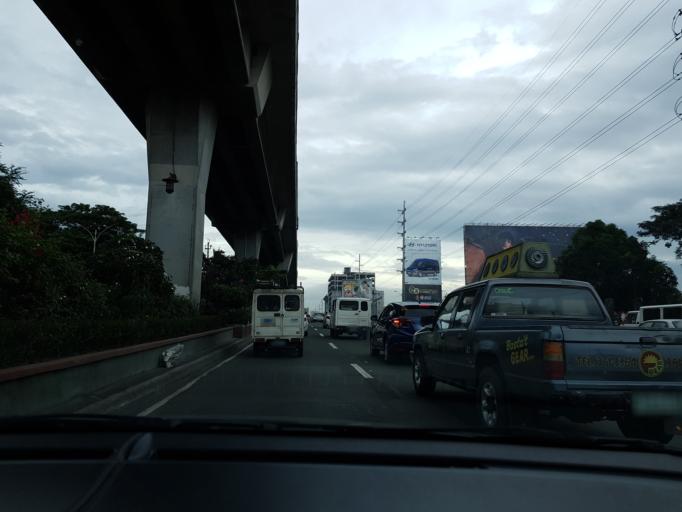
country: PH
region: Calabarzon
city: Del Monte
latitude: 14.6573
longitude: 120.9993
